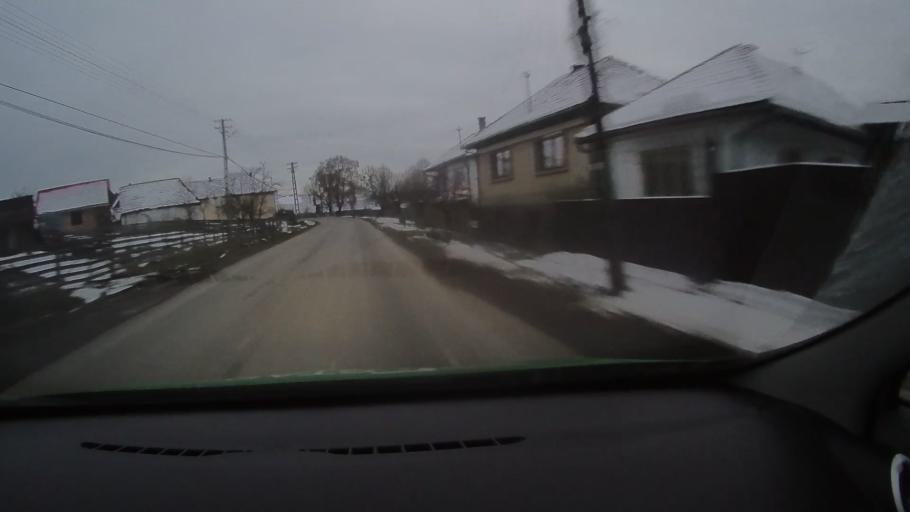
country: RO
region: Harghita
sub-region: Comuna Darjiu
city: Darjiu
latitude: 46.2113
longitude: 25.2402
